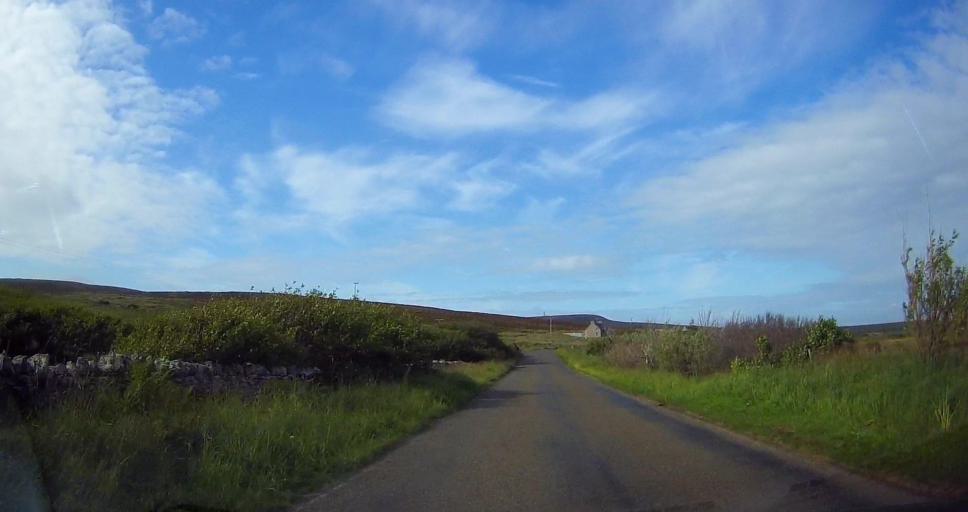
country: GB
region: Scotland
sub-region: Orkney Islands
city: Stromness
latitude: 58.7899
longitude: -3.2588
